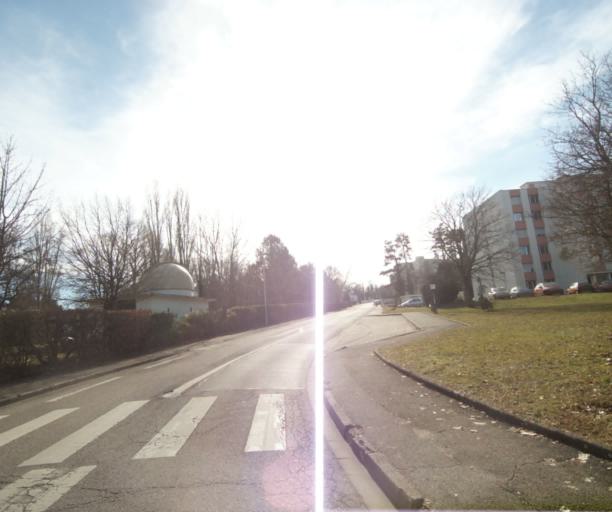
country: FR
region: Lorraine
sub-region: Departement de Meurthe-et-Moselle
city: Villers-les-Nancy
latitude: 48.6544
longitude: 6.1598
